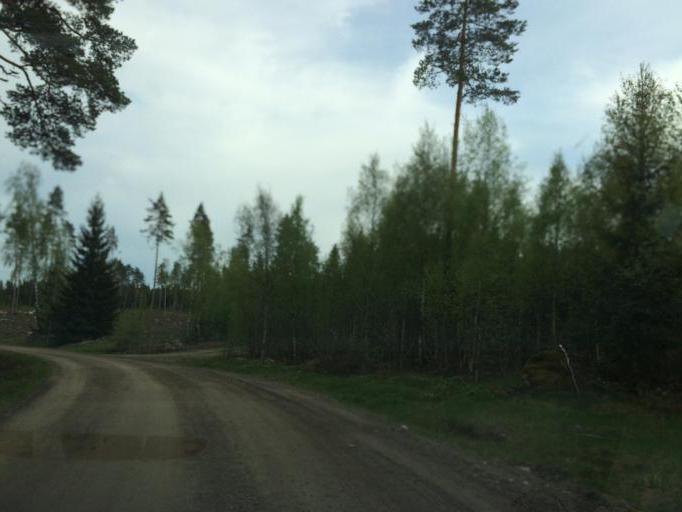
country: SE
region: Vaestmanland
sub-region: Kopings Kommun
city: Koping
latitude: 59.6126
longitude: 16.0470
